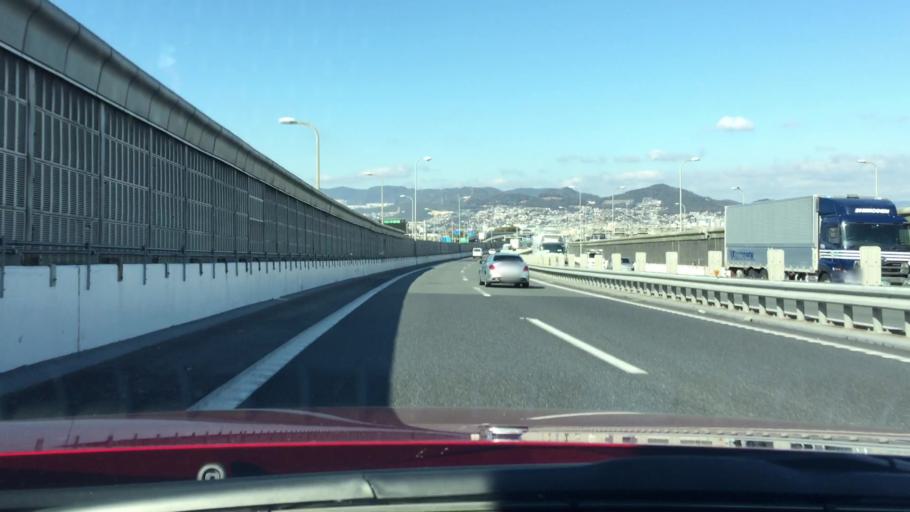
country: JP
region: Osaka
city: Ikeda
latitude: 34.8021
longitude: 135.4359
